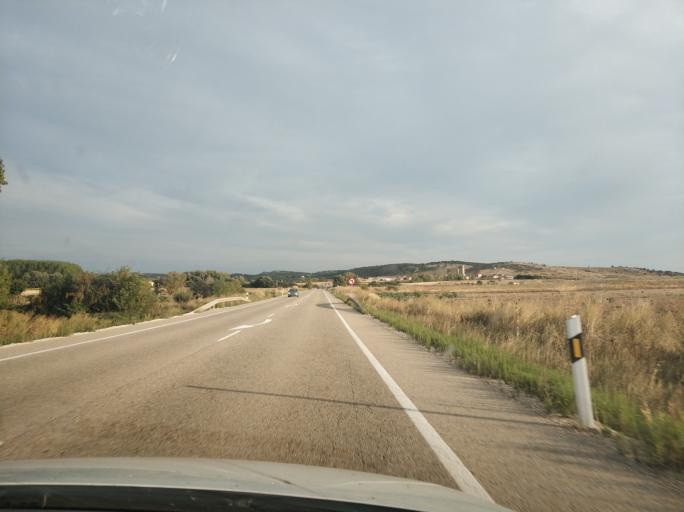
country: ES
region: Castille and Leon
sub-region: Provincia de Burgos
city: Hontoria de la Cantera
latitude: 42.1976
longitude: -3.6461
